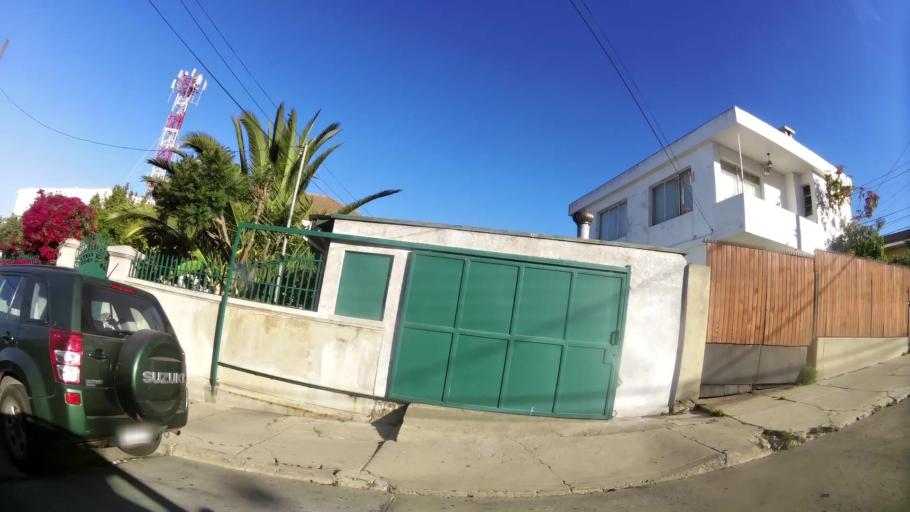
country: CL
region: Valparaiso
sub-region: Provincia de Valparaiso
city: Vina del Mar
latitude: -33.0315
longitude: -71.5793
